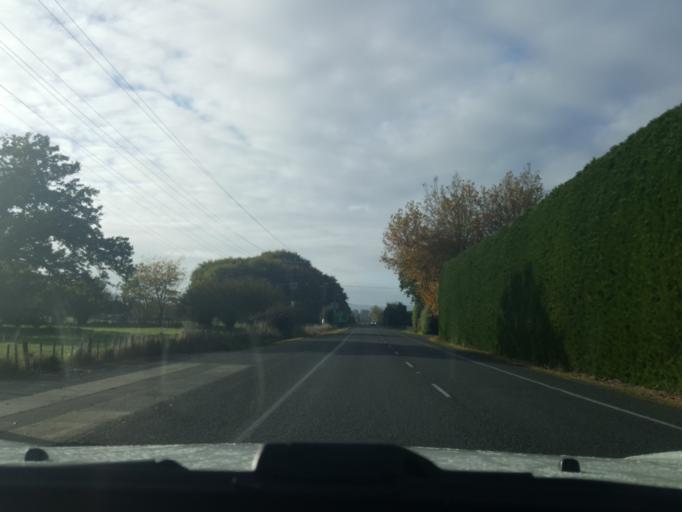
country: NZ
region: Waikato
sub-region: Hamilton City
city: Hamilton
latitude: -37.7771
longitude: 175.3819
